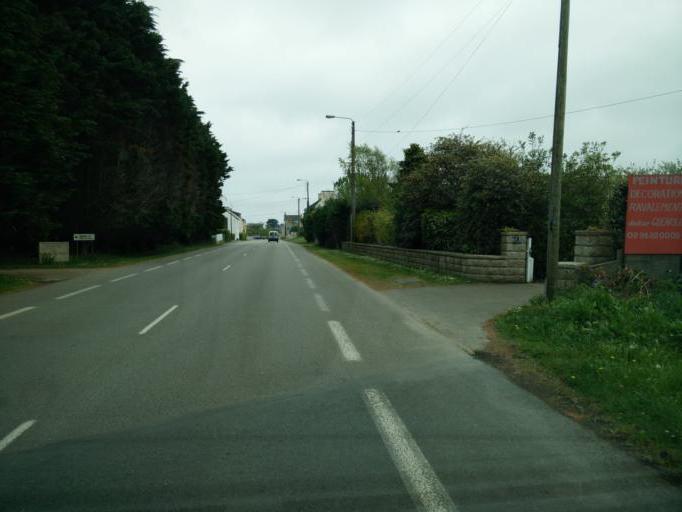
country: FR
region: Brittany
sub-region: Departement du Finistere
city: Plobannalec-Lesconil
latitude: 47.8042
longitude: -4.2232
